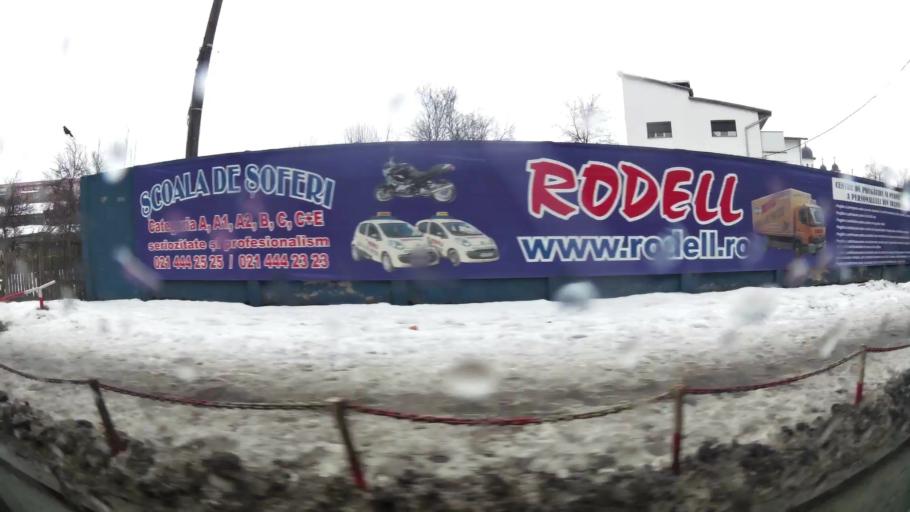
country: RO
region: Ilfov
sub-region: Comuna Chiajna
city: Rosu
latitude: 44.4120
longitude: 26.0180
